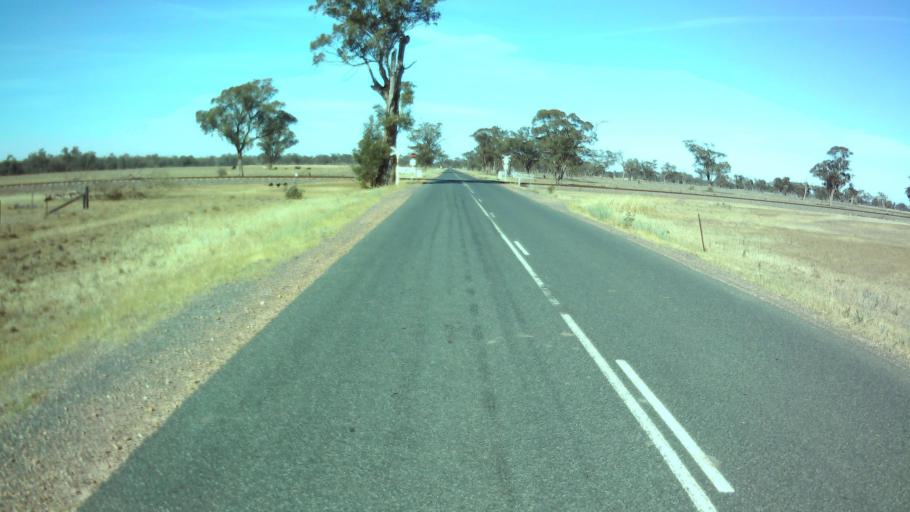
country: AU
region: New South Wales
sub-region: Weddin
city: Grenfell
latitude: -34.1062
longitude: 147.8629
